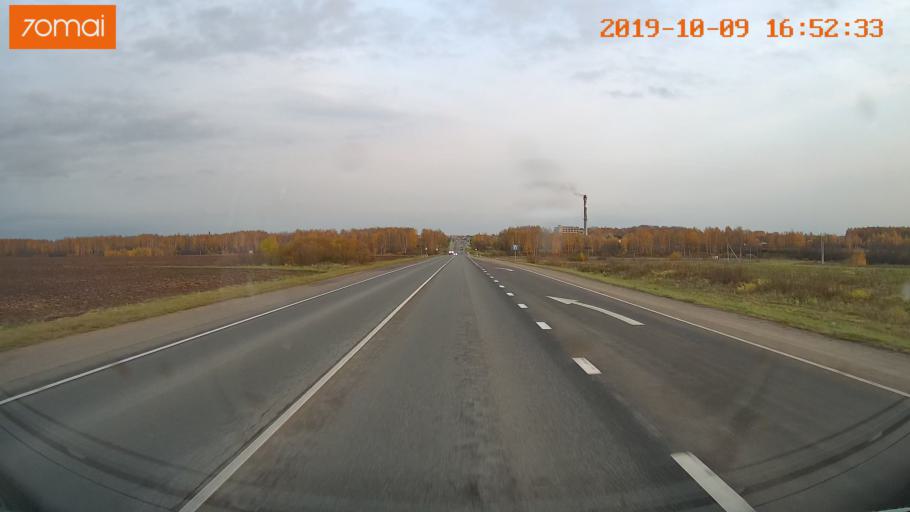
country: RU
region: Ivanovo
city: Privolzhsk
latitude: 57.3802
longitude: 41.2498
